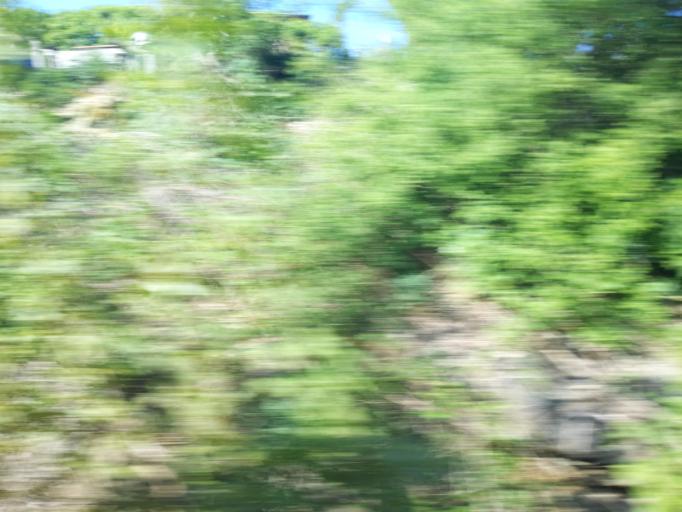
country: DE
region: Saxony
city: Bautzen
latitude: 51.1770
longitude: 14.4061
